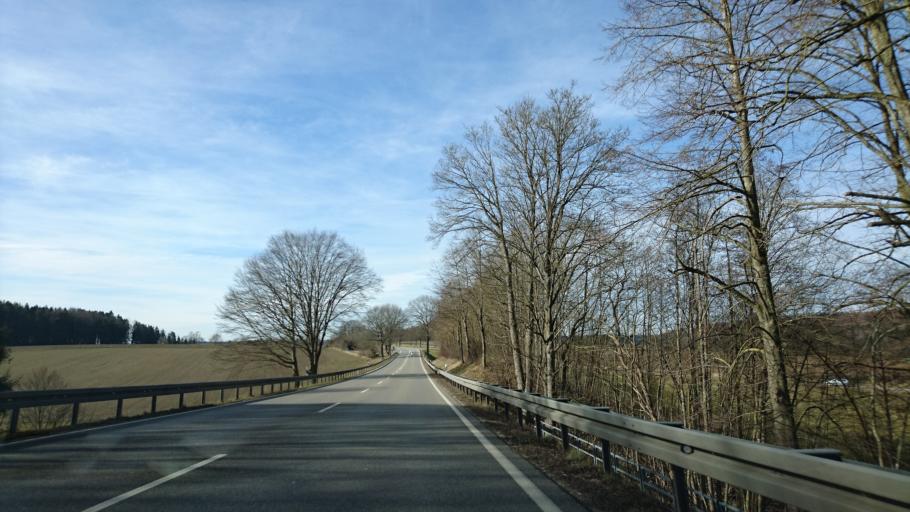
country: DE
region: Bavaria
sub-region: Swabia
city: Krumbach
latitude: 48.2449
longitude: 10.3884
